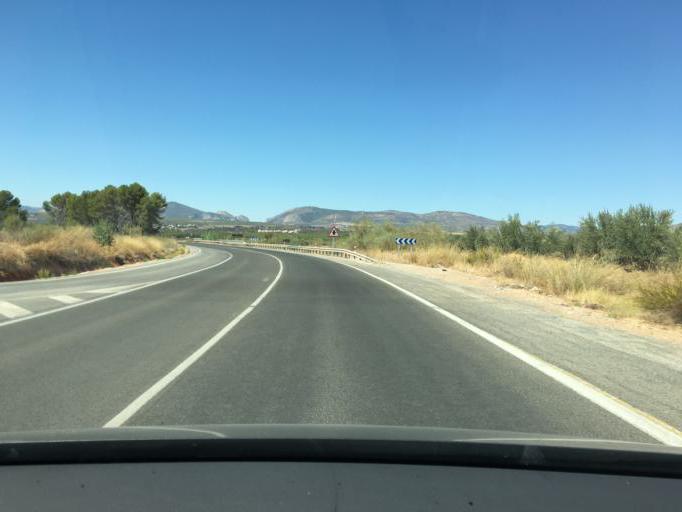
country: ES
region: Andalusia
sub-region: Provincia de Granada
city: Albolote
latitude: 37.2668
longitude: -3.6636
